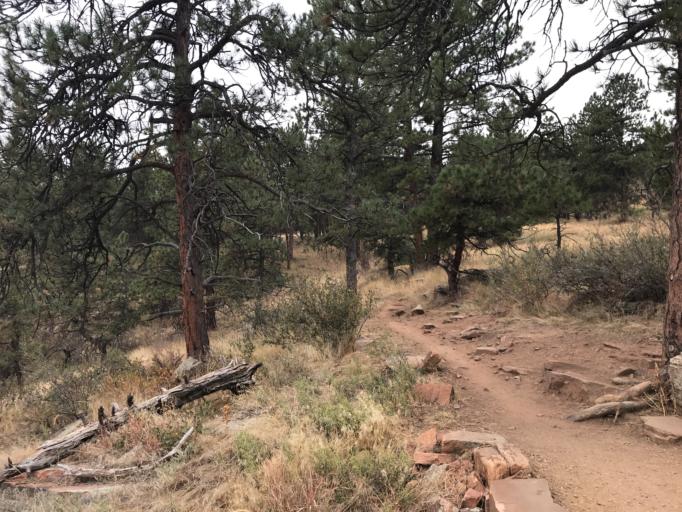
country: US
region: Colorado
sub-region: Boulder County
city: Lyons
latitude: 40.1780
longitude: -105.2885
